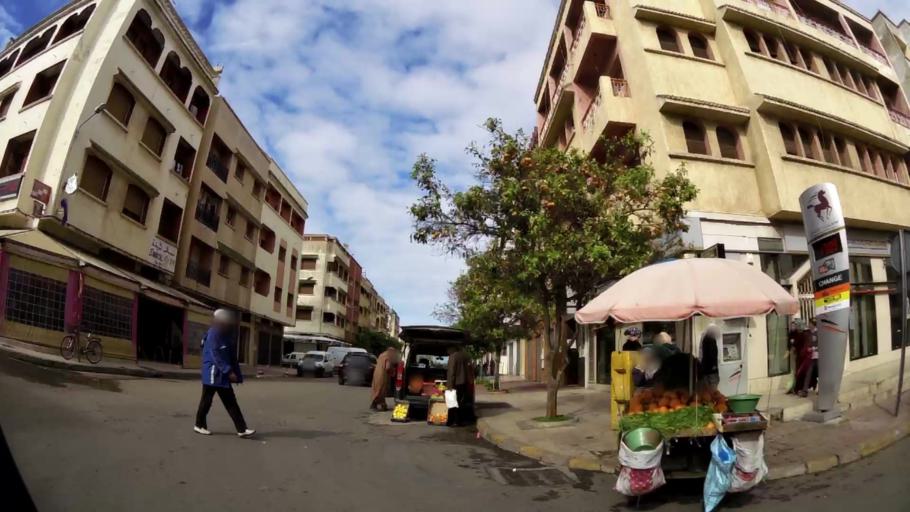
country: MA
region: Grand Casablanca
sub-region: Mohammedia
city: Mohammedia
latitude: 33.6924
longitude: -7.3850
